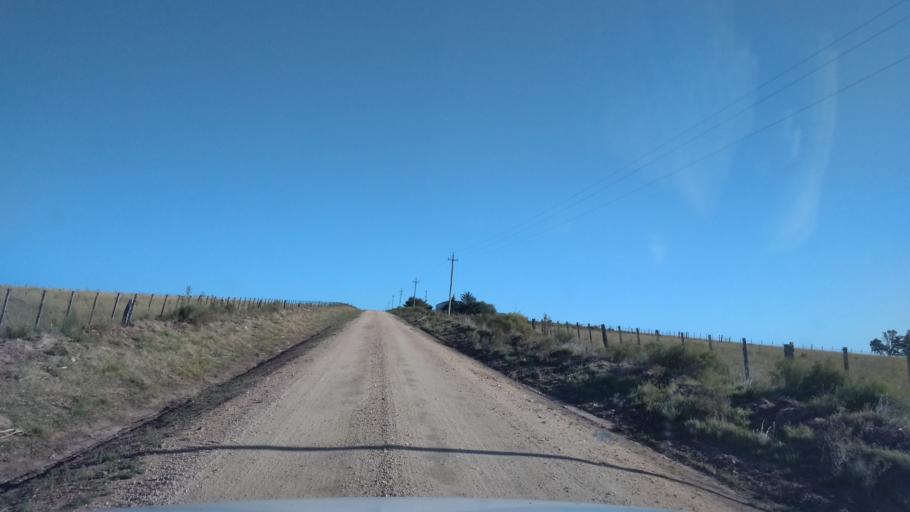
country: UY
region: Florida
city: Casupa
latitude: -34.0189
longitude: -55.7856
